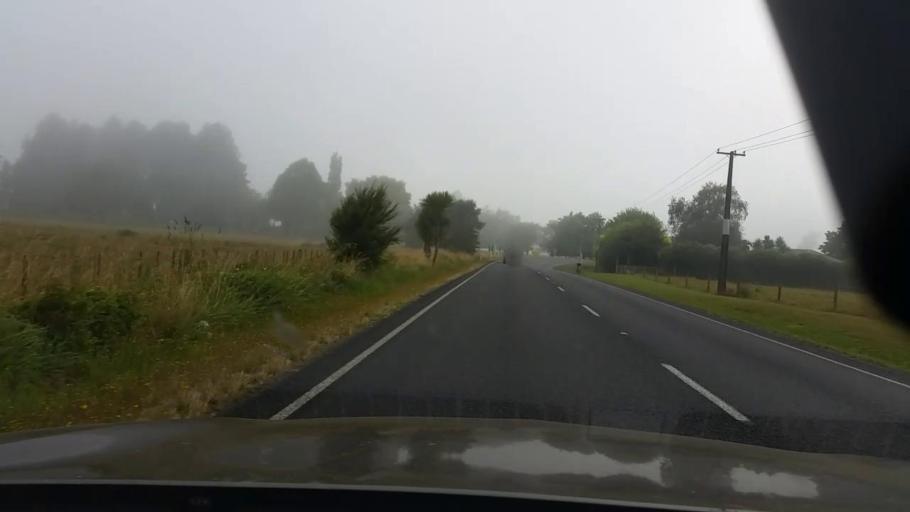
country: NZ
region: Waikato
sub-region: Waikato District
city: Ngaruawahia
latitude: -37.6389
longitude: 175.2959
